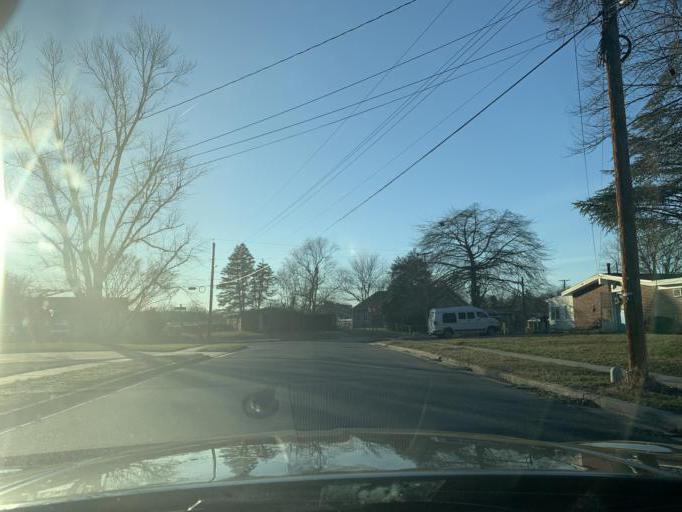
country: US
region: Maryland
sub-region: Anne Arundel County
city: South Gate
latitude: 39.1448
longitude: -76.6242
